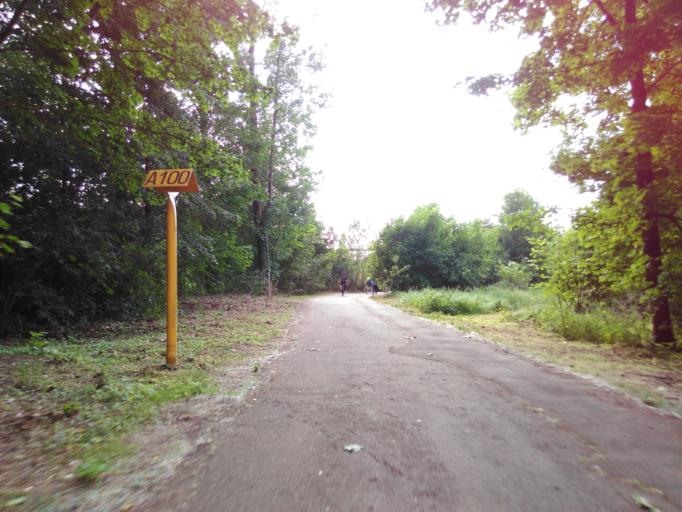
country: LU
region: Luxembourg
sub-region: Canton d'Esch-sur-Alzette
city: Schifflange
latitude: 49.5077
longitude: 6.0019
